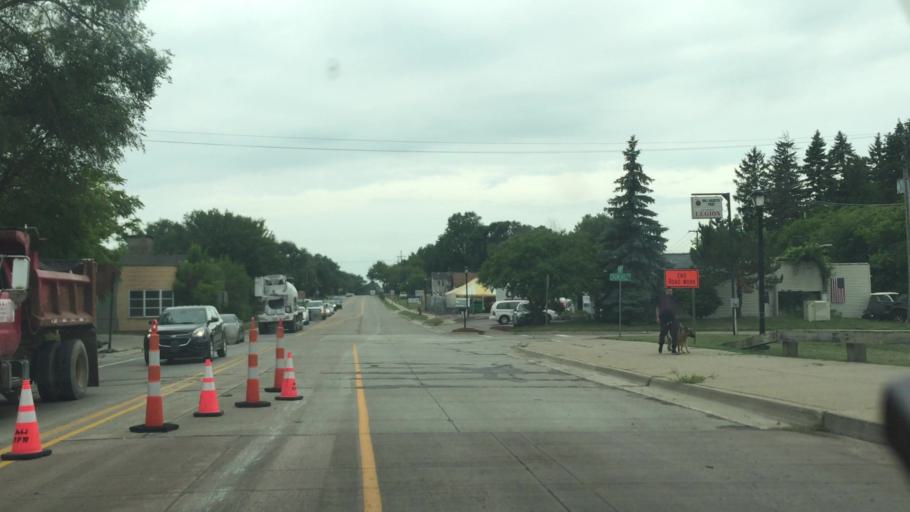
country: US
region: Michigan
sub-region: Oakland County
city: Bloomfield Hills
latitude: 42.6336
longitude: -83.2246
